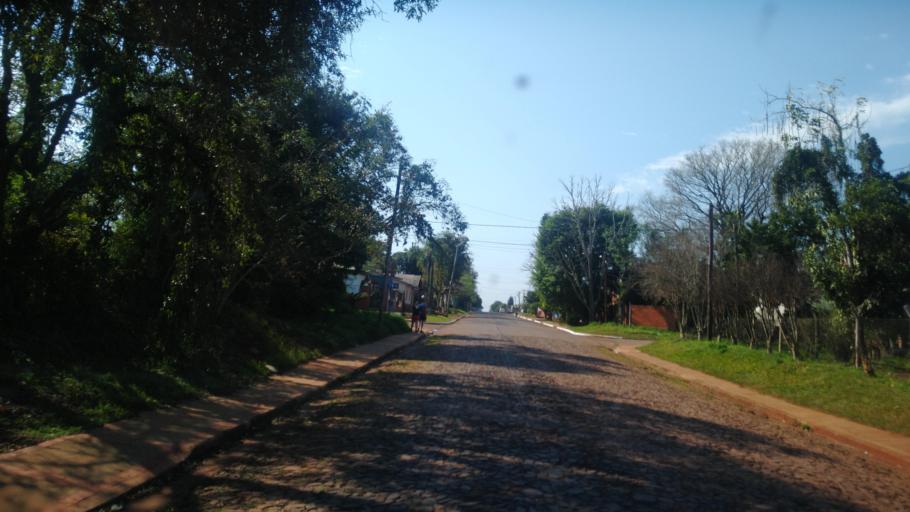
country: AR
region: Misiones
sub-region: Departamento de San Ignacio
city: San Ignacio
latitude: -27.2597
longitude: -55.5428
